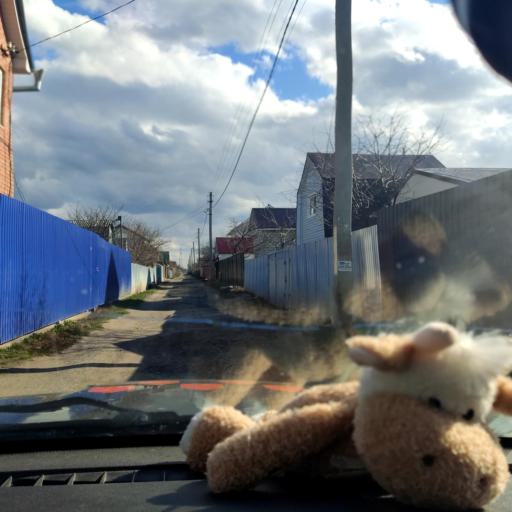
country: RU
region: Samara
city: Tol'yatti
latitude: 53.5952
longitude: 49.3086
